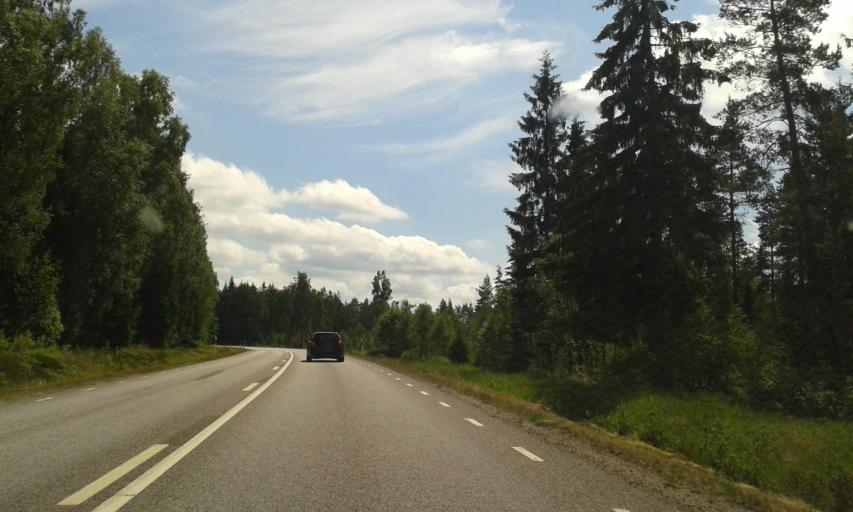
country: SE
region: Joenkoeping
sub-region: Varnamo Kommun
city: Rydaholm
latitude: 56.9780
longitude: 14.3082
